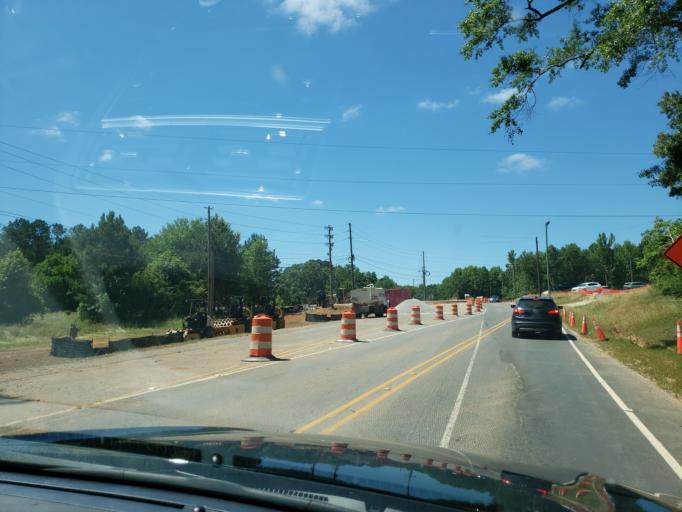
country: US
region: Alabama
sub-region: Lee County
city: Auburn
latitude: 32.6670
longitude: -85.4895
